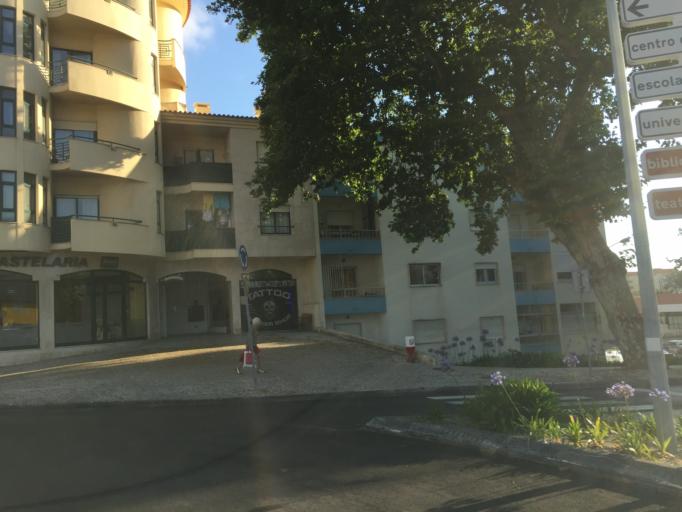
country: PT
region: Leiria
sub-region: Caldas da Rainha
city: Caldas da Rainha
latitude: 39.4024
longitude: -9.1404
